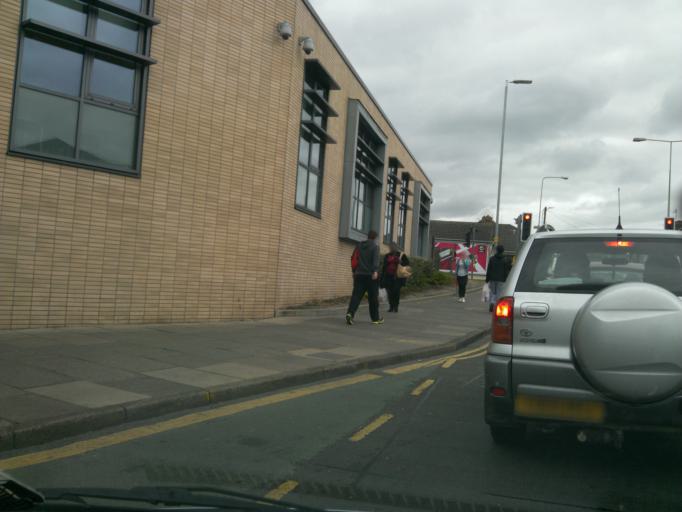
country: GB
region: England
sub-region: Essex
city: Colchester
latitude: 51.8861
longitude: 0.9049
